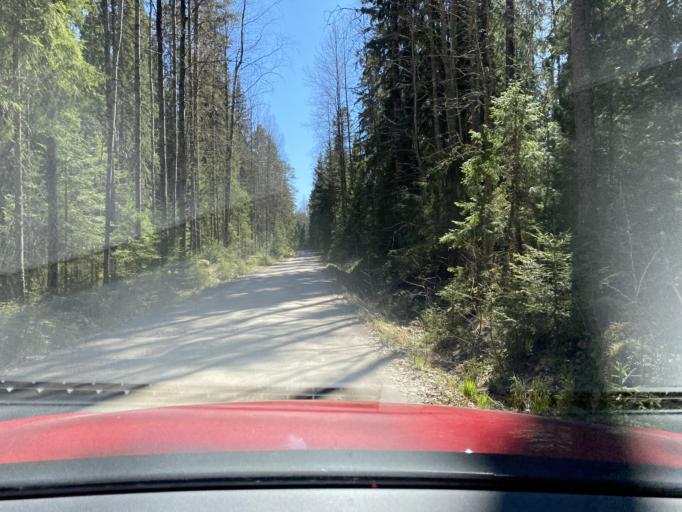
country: FI
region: Uusimaa
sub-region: Helsinki
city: Kaerkoelae
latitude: 60.6583
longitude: 23.8699
